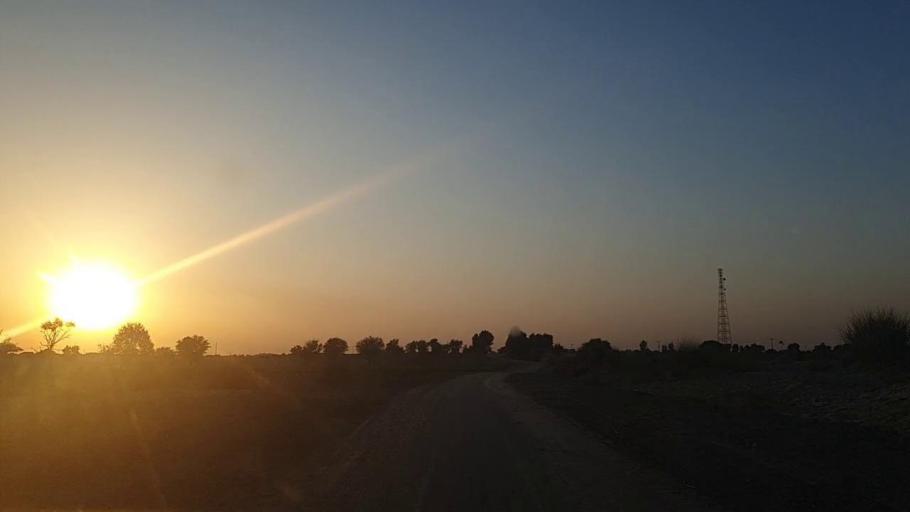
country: PK
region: Sindh
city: Jam Sahib
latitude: 26.3668
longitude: 68.7131
